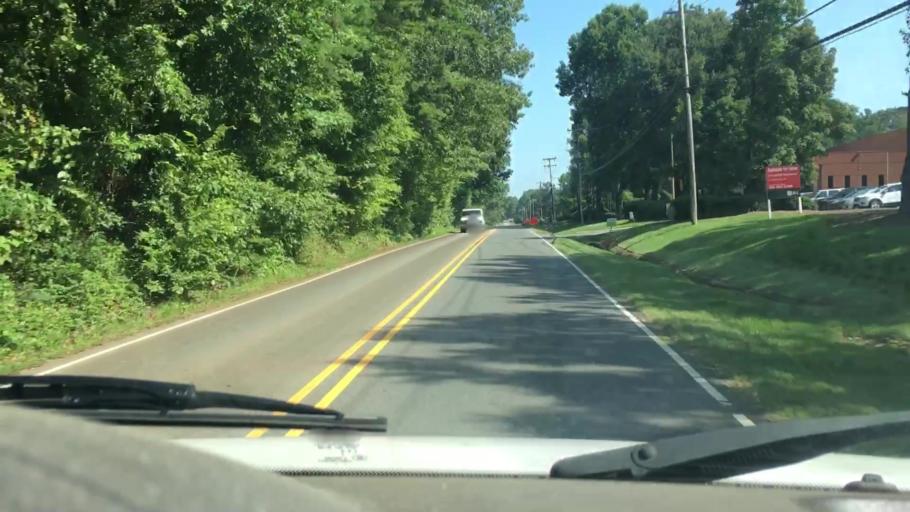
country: US
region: North Carolina
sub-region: Mecklenburg County
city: Huntersville
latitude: 35.3193
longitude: -80.8524
